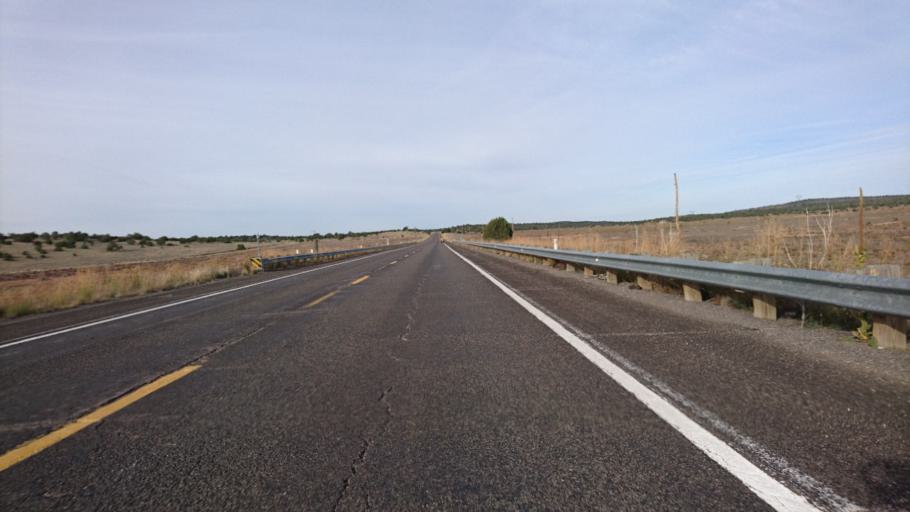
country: US
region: Arizona
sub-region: Mohave County
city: Peach Springs
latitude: 35.5532
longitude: -113.3381
